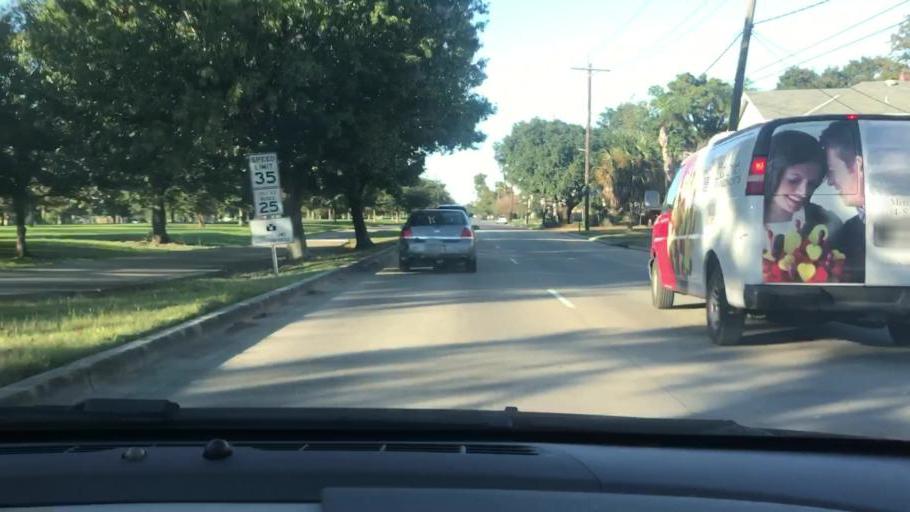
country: US
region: Louisiana
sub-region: Jefferson Parish
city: Metairie
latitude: 30.0059
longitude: -90.1146
